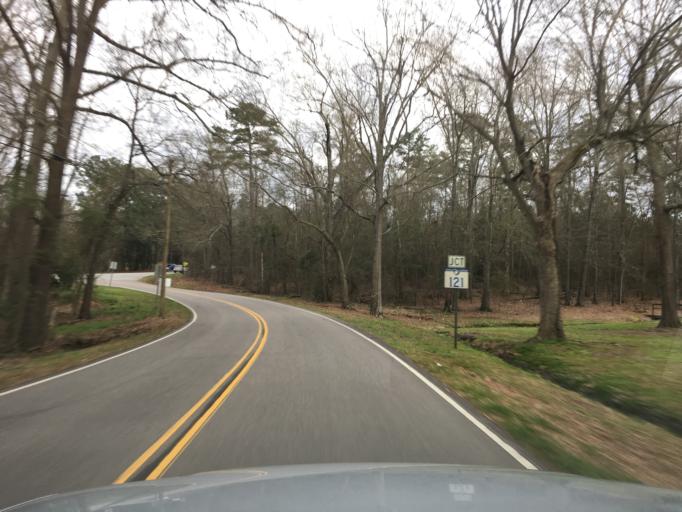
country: US
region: South Carolina
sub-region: Saluda County
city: Saluda
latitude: 33.9950
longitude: -81.7721
